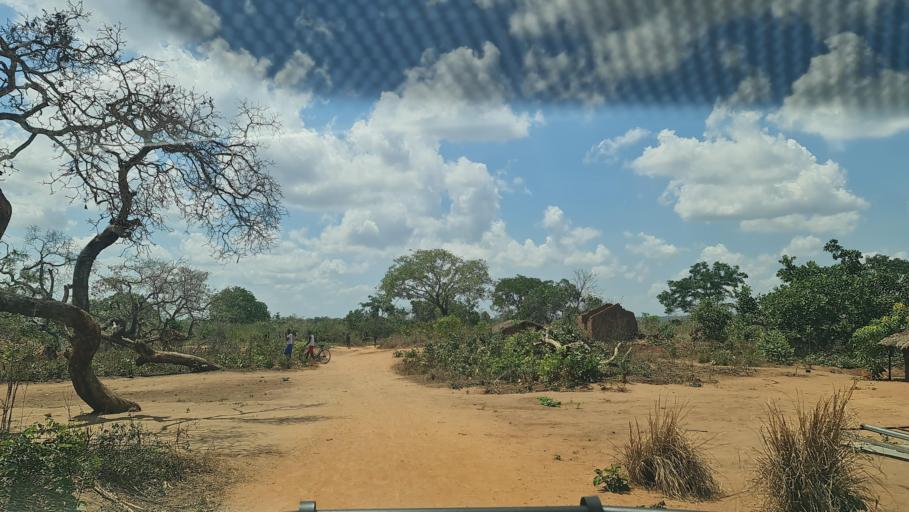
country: MZ
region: Nampula
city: Ilha de Mocambique
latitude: -15.0530
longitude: 40.3304
